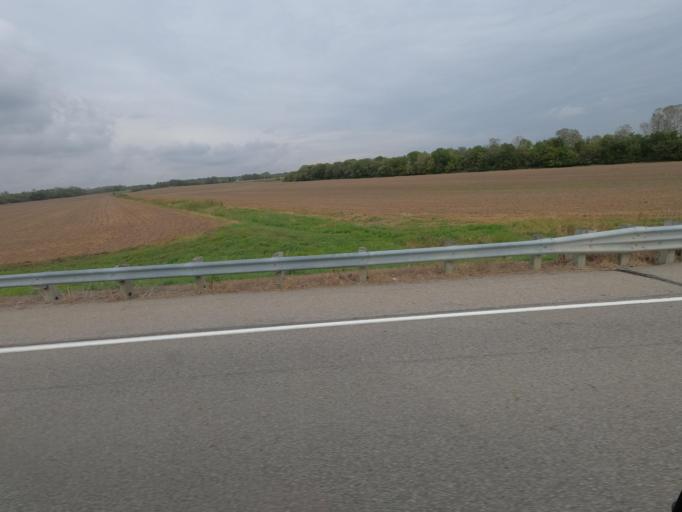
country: US
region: Iowa
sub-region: Jefferson County
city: Fairfield
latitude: 40.8944
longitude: -92.1819
